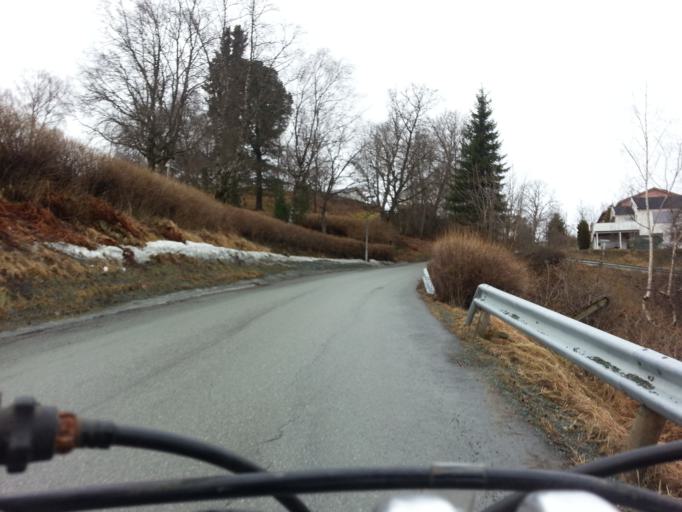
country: NO
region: Sor-Trondelag
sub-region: Trondheim
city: Trondheim
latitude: 63.4126
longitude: 10.3805
